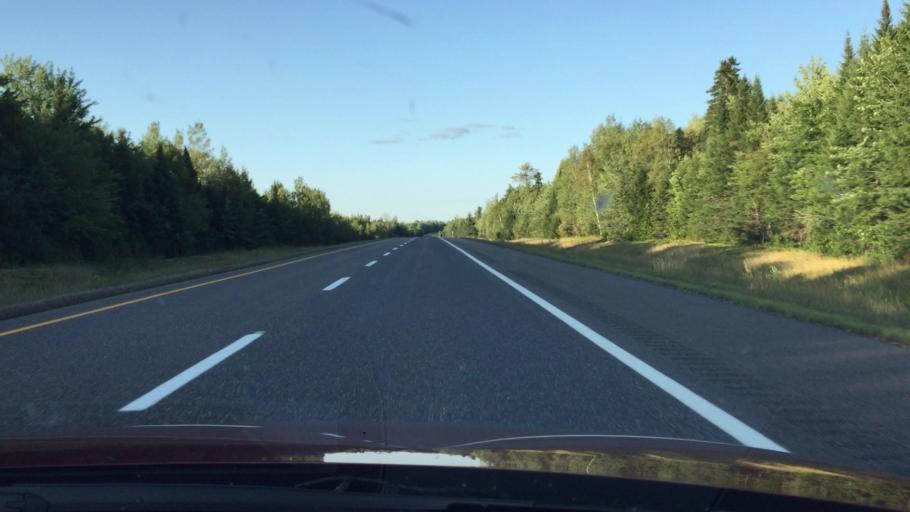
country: US
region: Maine
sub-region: Penobscot County
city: Patten
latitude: 46.0767
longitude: -68.2168
